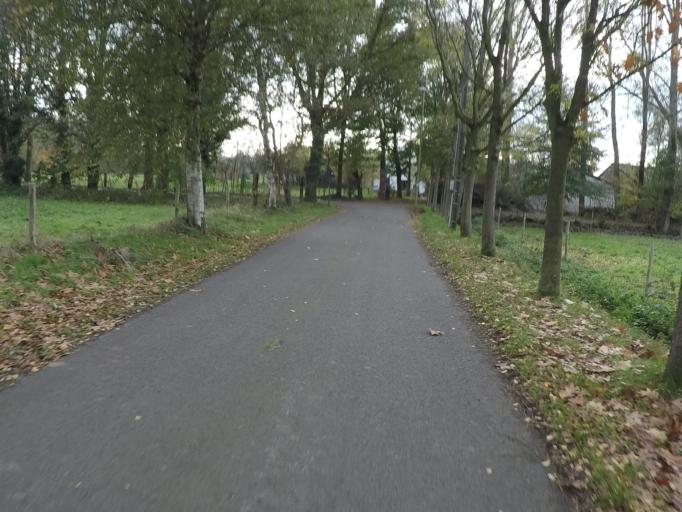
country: BE
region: Flanders
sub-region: Provincie Antwerpen
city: Berlaar
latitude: 51.1382
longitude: 4.6630
